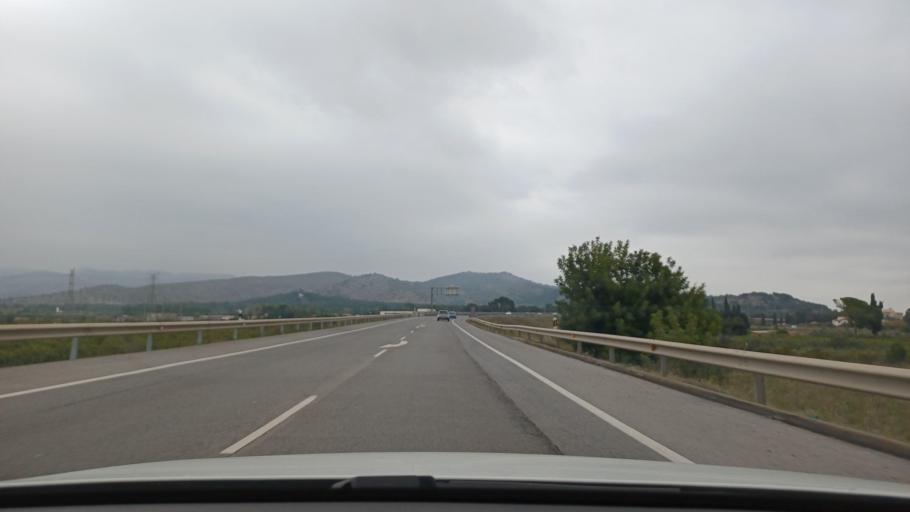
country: ES
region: Valencia
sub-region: Provincia de Castello
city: Borriol
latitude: 39.9984
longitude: -0.0874
